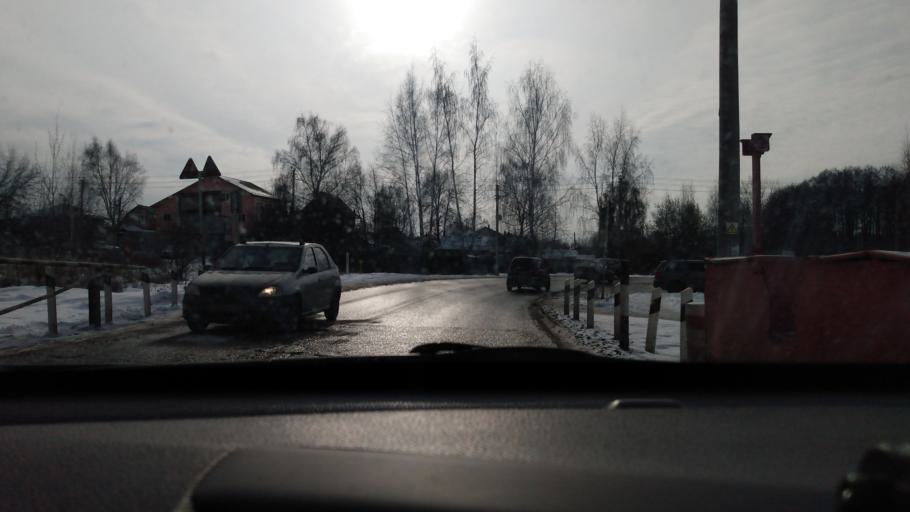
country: RU
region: Moskovskaya
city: Chornaya
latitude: 55.7532
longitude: 38.0621
